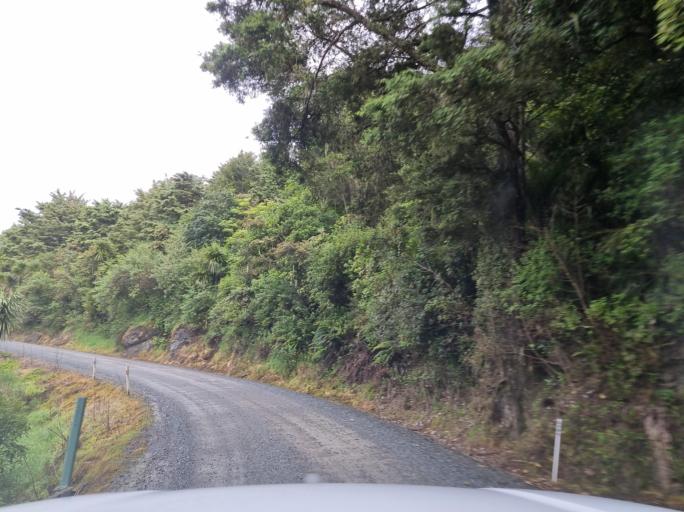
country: NZ
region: Northland
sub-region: Whangarei
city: Ruakaka
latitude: -35.9355
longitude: 174.3541
